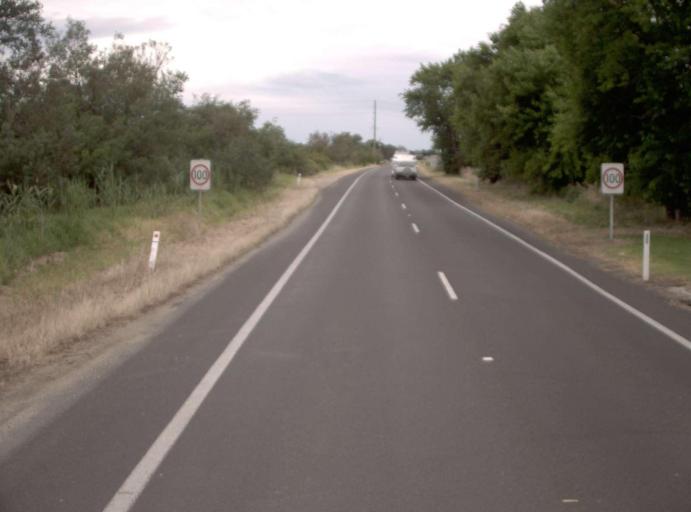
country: AU
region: Victoria
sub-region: East Gippsland
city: Bairnsdale
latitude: -37.8306
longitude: 147.6405
